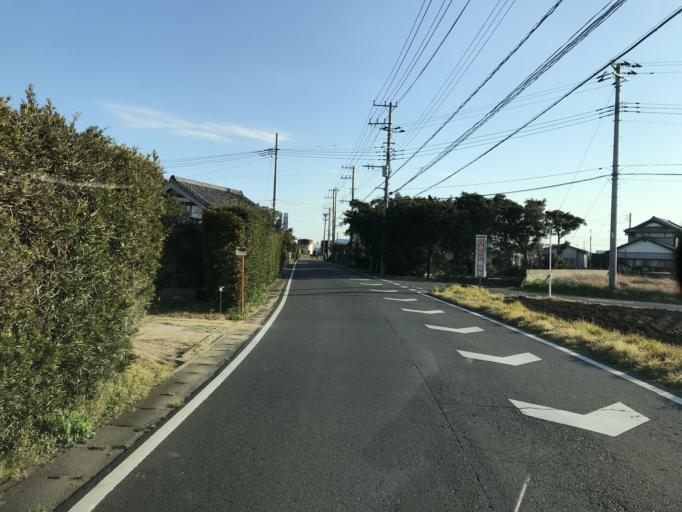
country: JP
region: Chiba
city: Yokaichiba
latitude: 35.6762
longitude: 140.5953
